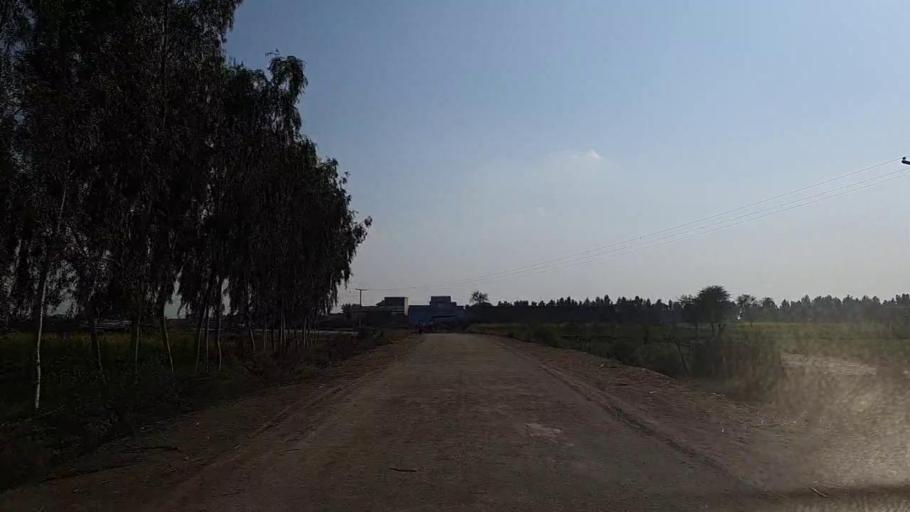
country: PK
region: Sindh
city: Jam Sahib
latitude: 26.2777
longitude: 68.5828
